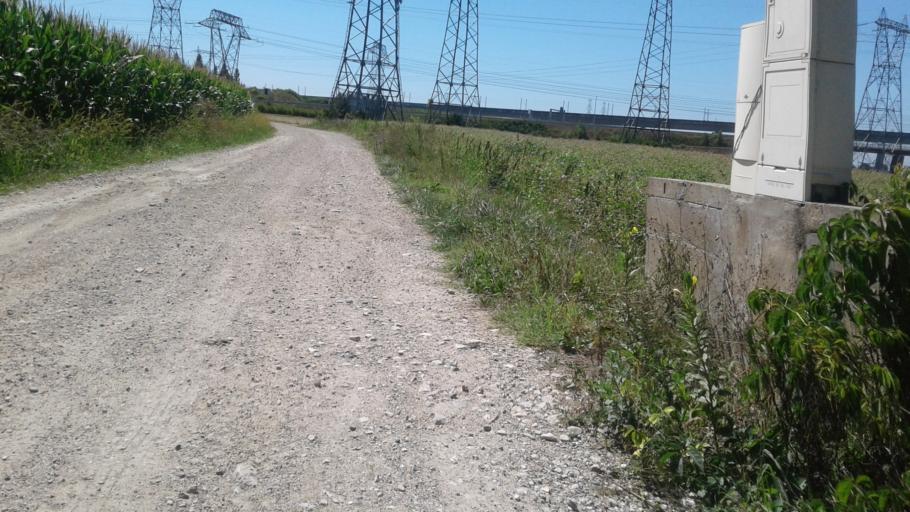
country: FR
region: Rhone-Alpes
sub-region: Departement de l'Ain
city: La Boisse
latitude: 45.8373
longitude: 5.0282
